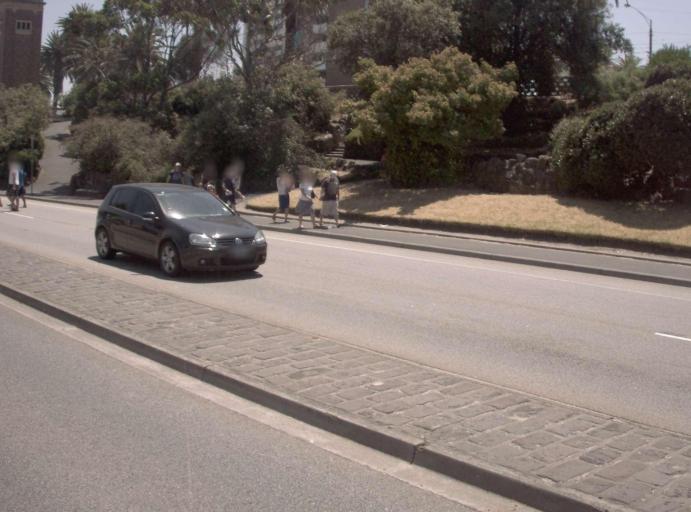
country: AU
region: Victoria
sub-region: Port Phillip
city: St Kilda West
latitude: -37.8657
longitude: 144.9734
